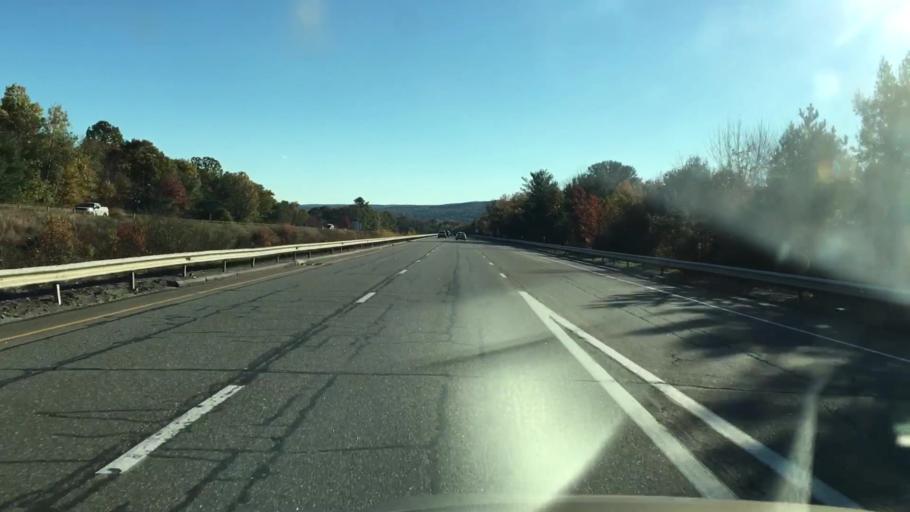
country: US
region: Connecticut
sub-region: Litchfield County
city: Torrington
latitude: 41.8247
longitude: -73.1096
